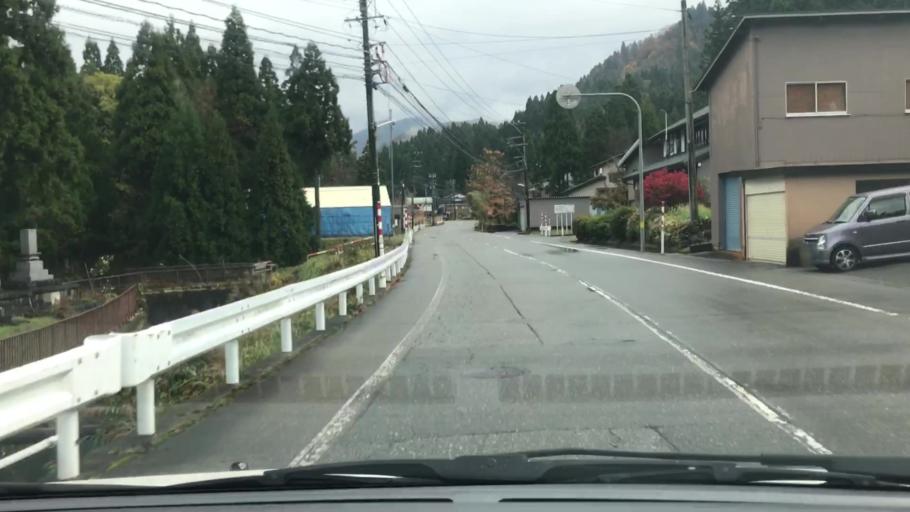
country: JP
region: Toyama
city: Kamiichi
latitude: 36.5703
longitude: 137.3504
